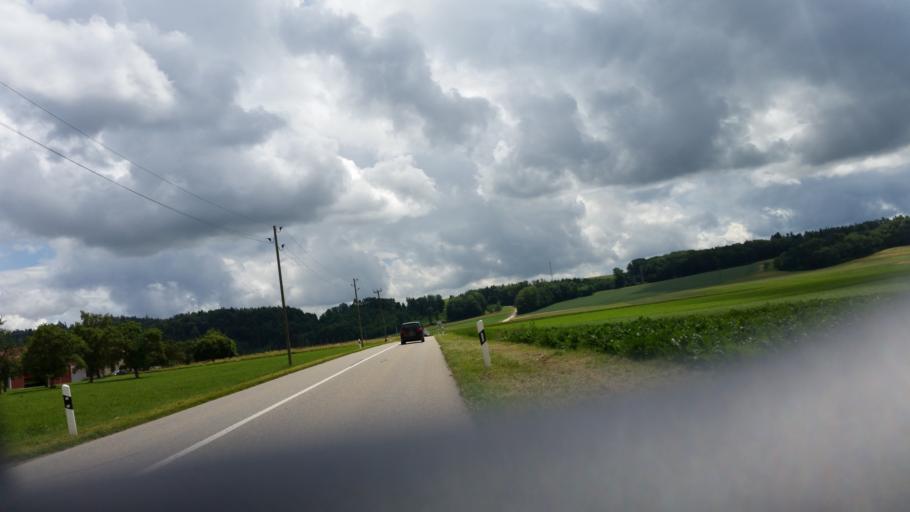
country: CH
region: Vaud
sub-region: Jura-Nord vaudois District
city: Yverdon-les-Bains
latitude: 46.7568
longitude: 6.6707
